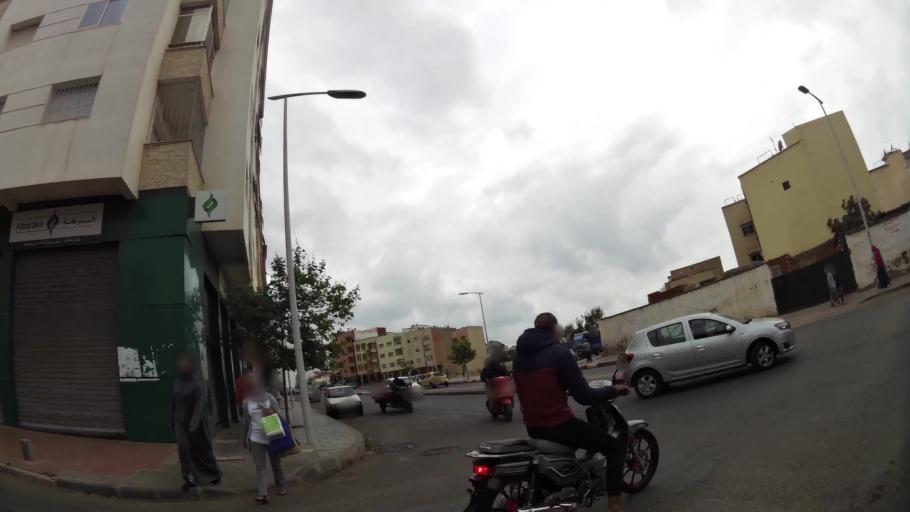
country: MA
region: Rabat-Sale-Zemmour-Zaer
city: Sale
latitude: 34.0417
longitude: -6.8065
